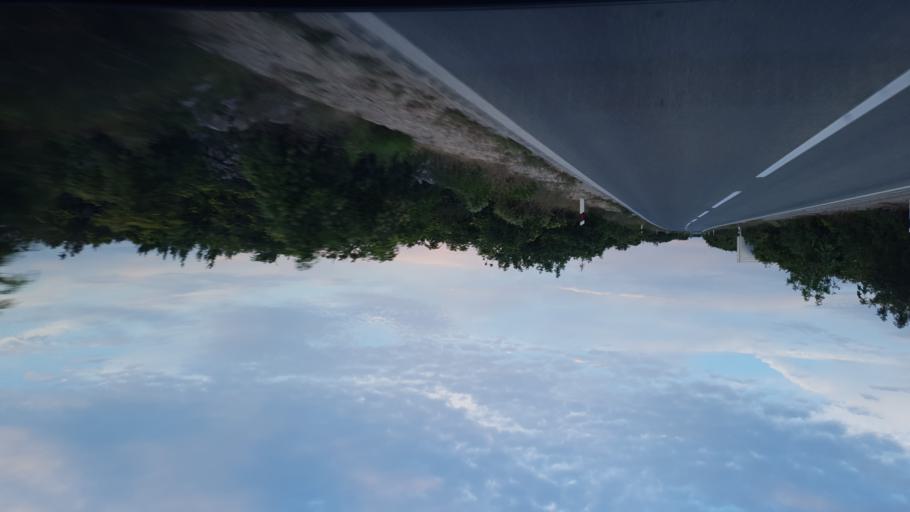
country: HR
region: Primorsko-Goranska
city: Punat
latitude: 45.0424
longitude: 14.6401
